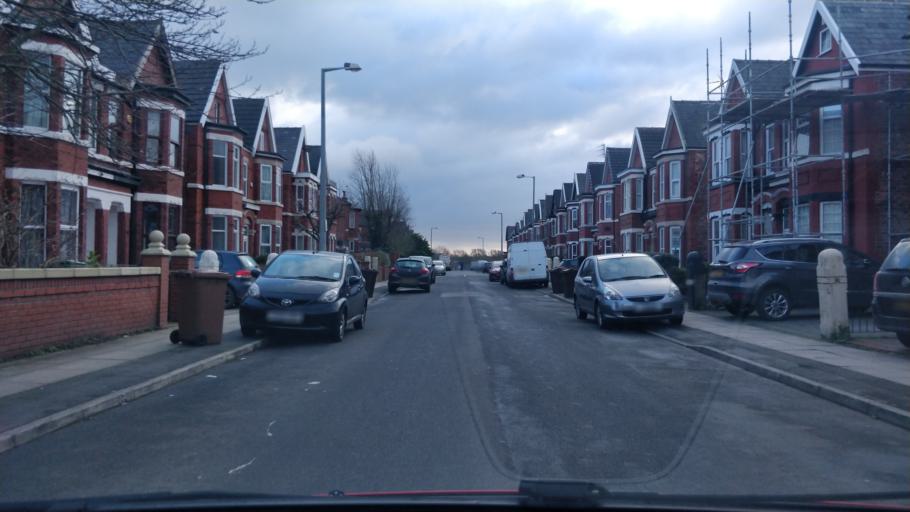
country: GB
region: England
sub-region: Sefton
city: Southport
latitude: 53.6352
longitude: -2.9941
